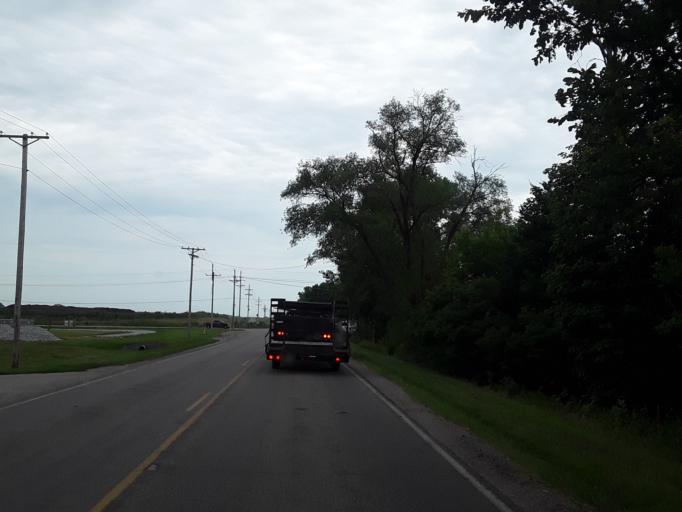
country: US
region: Nebraska
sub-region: Saunders County
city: Yutan
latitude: 41.2354
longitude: -96.3304
